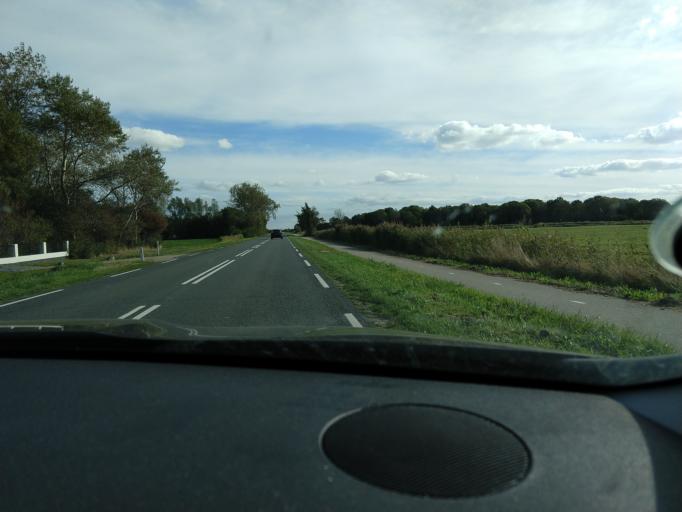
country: NL
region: Zeeland
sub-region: Gemeente Middelburg
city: Middelburg
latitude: 51.5404
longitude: 3.5322
